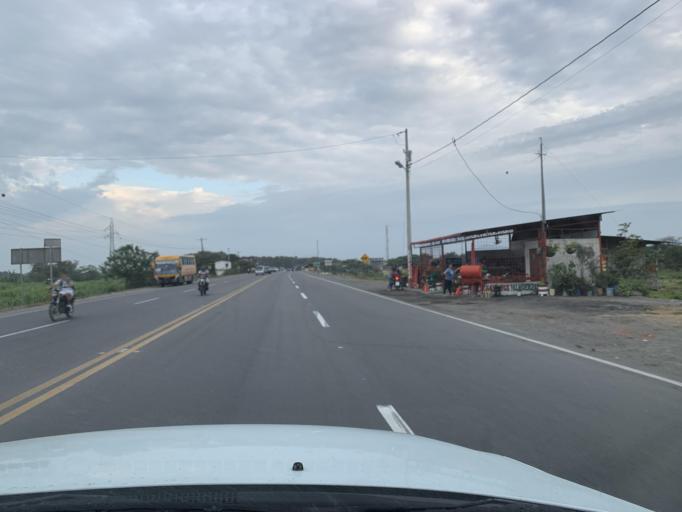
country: EC
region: Guayas
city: Yaguachi Nuevo
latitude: -2.2433
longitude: -79.6371
